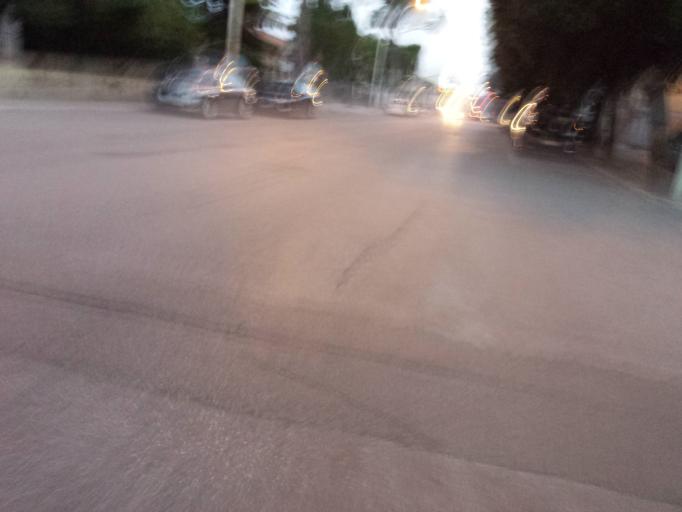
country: IT
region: Molise
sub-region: Provincia di Campobasso
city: Campobasso
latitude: 41.5678
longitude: 14.6731
